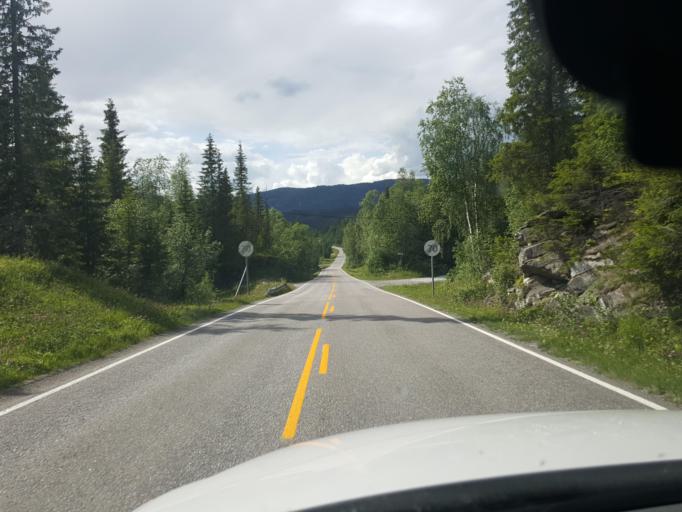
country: NO
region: Nordland
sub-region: Rana
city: Mo i Rana
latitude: 66.4074
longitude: 14.5108
